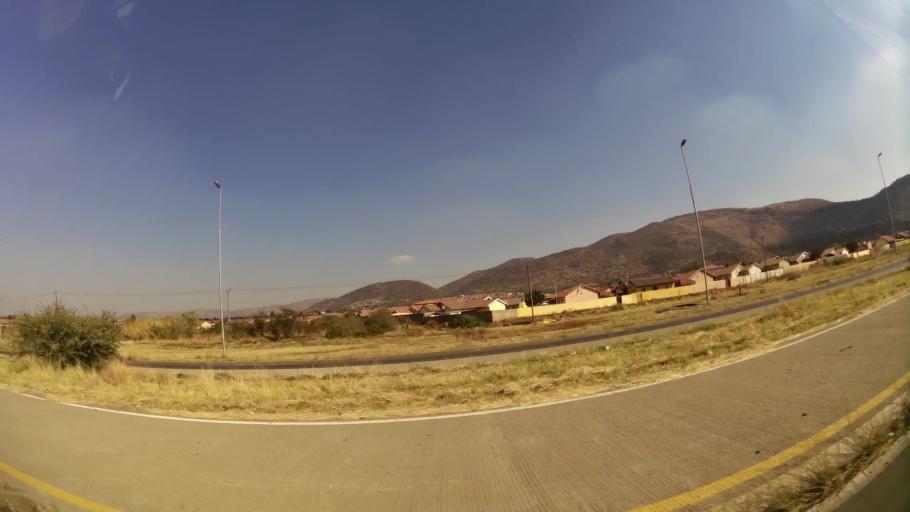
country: ZA
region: North-West
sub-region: Bojanala Platinum District Municipality
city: Rustenburg
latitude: -25.6434
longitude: 27.2067
